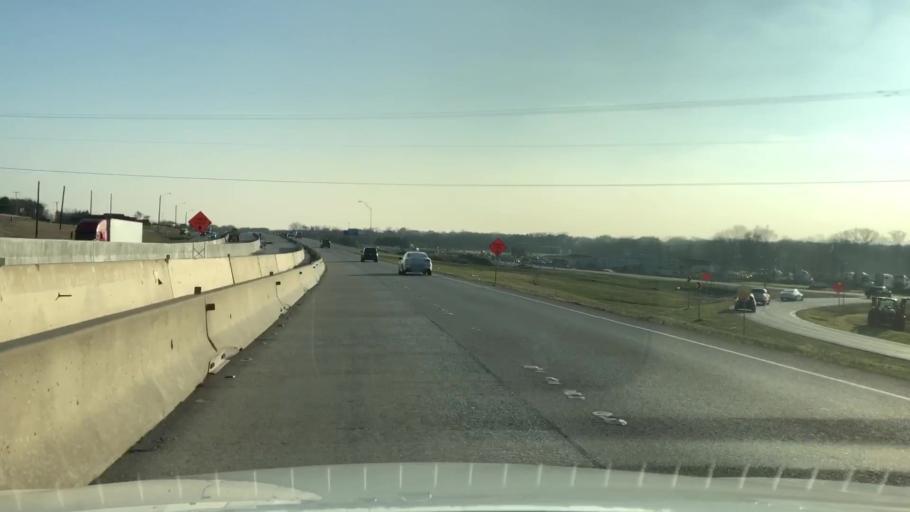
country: US
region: Texas
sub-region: Ellis County
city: Waxahachie
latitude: 32.4126
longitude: -96.8719
